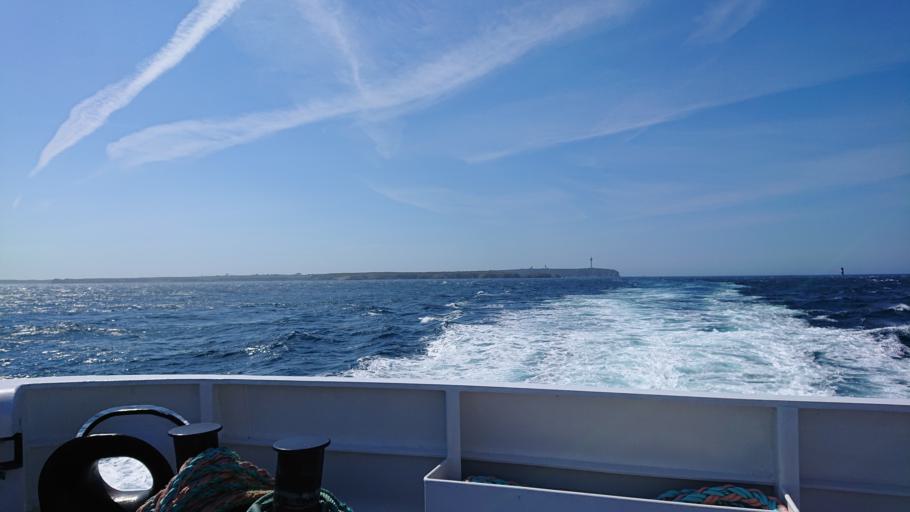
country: FR
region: Brittany
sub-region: Departement du Finistere
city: Porspoder
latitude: 48.4525
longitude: -5.0093
